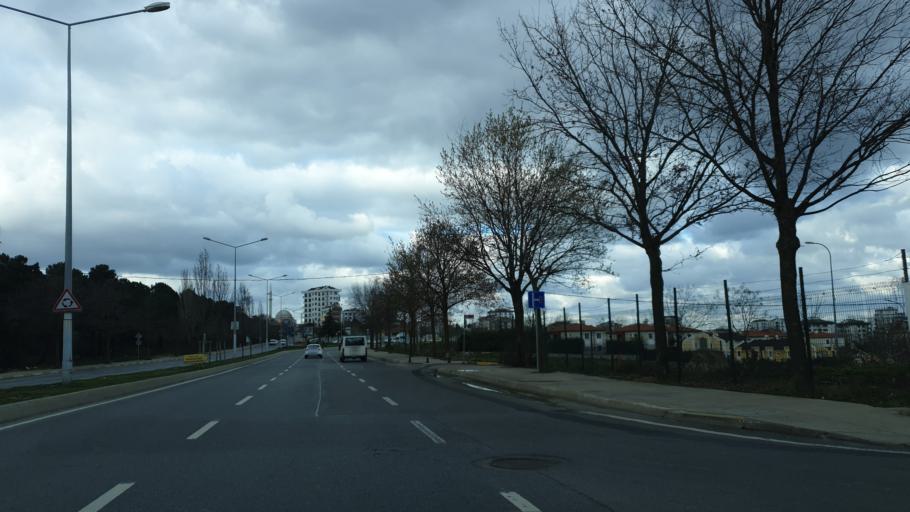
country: TR
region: Istanbul
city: Sultanbeyli
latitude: 40.9300
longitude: 29.2733
